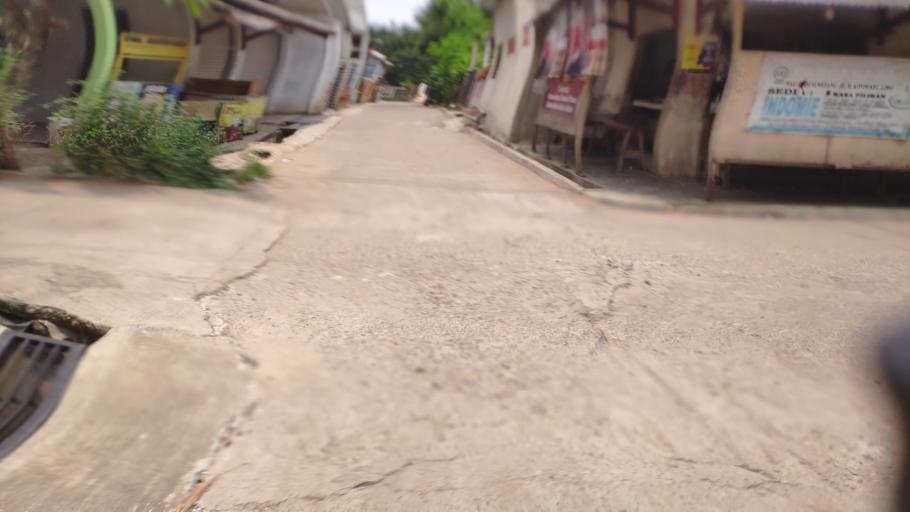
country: ID
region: West Java
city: Sawangan
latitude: -6.3818
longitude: 106.7895
